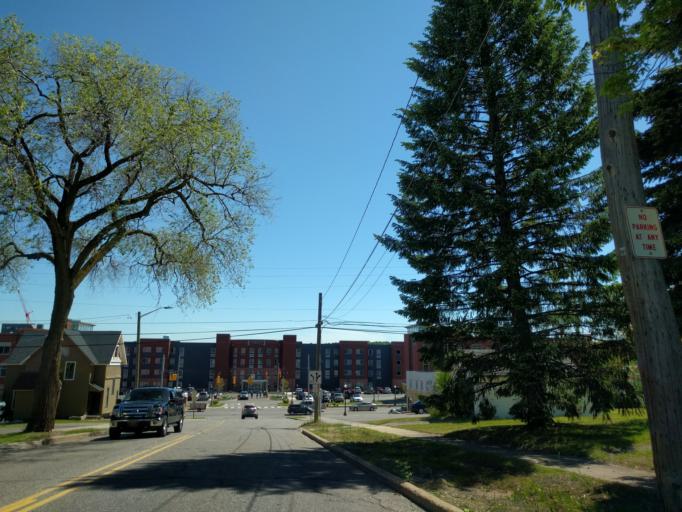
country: US
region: Michigan
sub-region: Marquette County
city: Marquette
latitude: 46.5467
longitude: -87.4123
